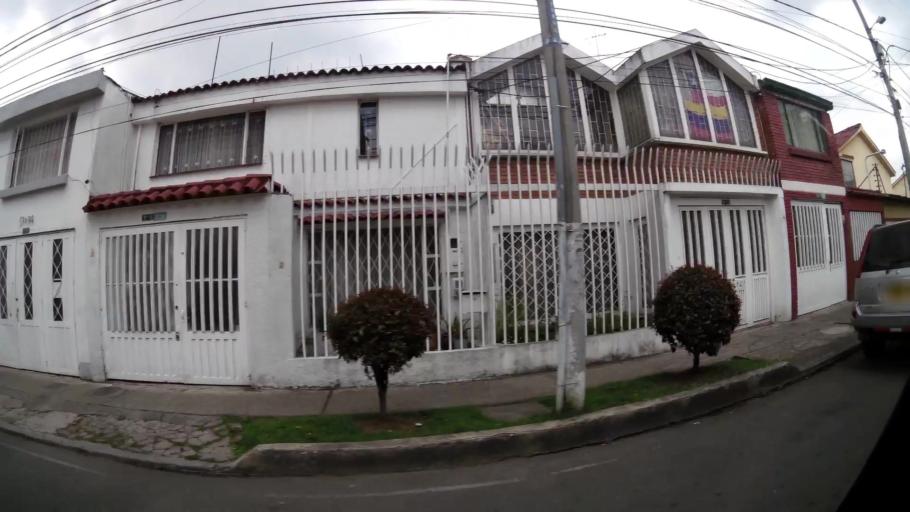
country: CO
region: Bogota D.C.
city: Barrio San Luis
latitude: 4.7417
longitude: -74.0440
